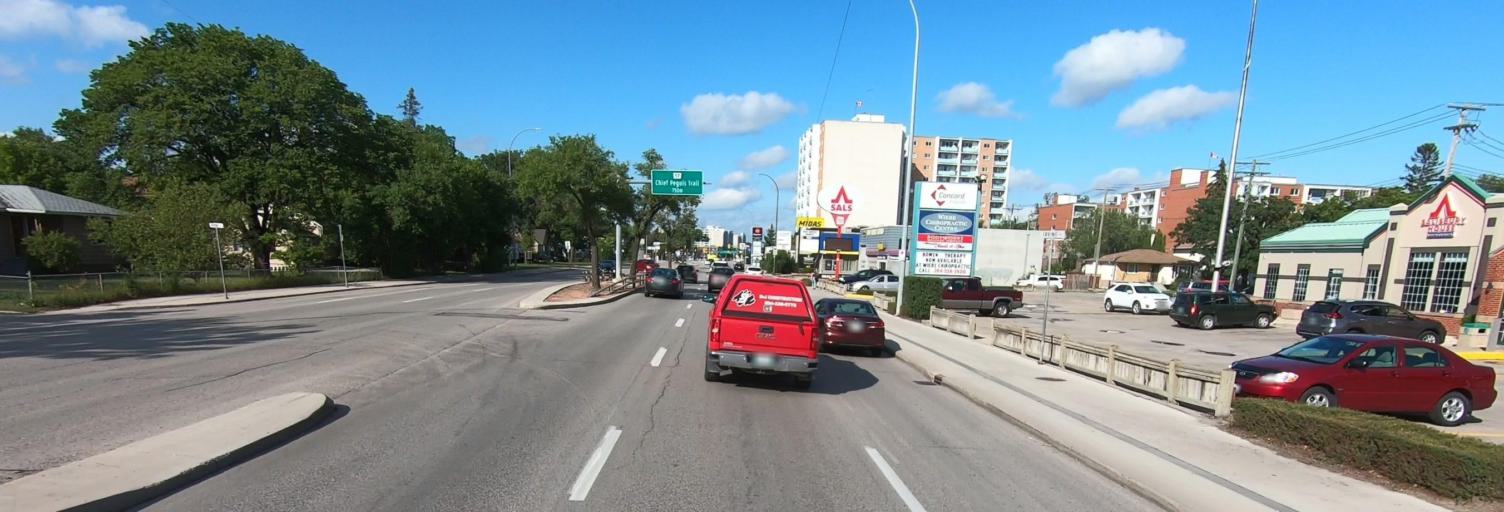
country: CA
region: Manitoba
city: Winnipeg
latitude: 49.9417
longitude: -97.0894
